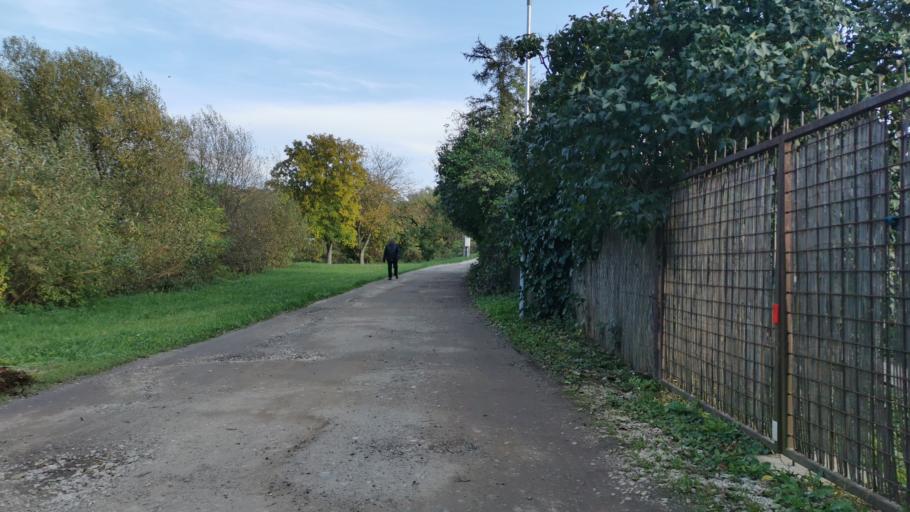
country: SK
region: Trnavsky
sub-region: Okres Skalica
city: Skalica
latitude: 48.8264
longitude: 17.2241
